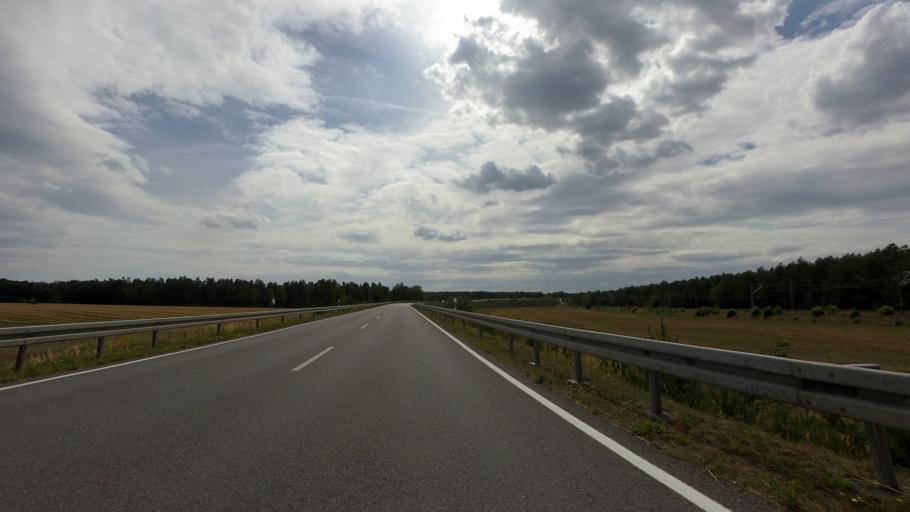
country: DE
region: Brandenburg
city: Spremberg
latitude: 51.5879
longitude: 14.3515
